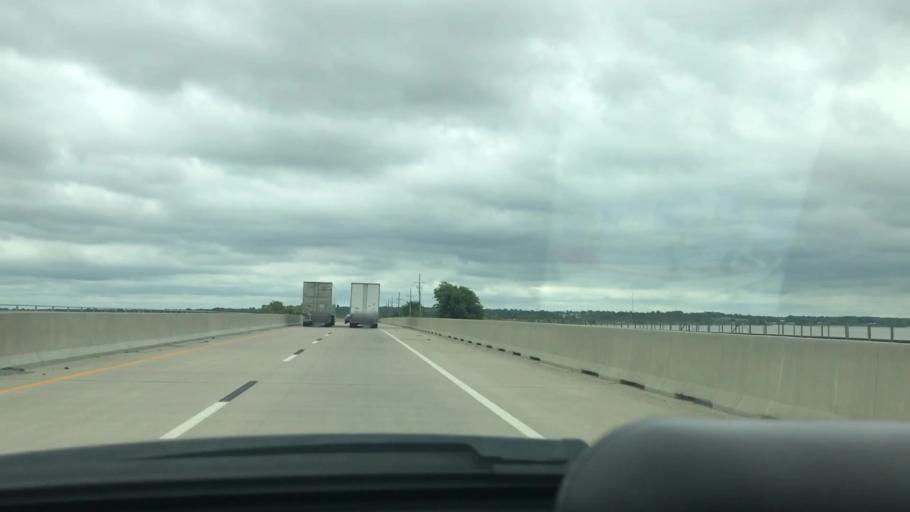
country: US
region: Oklahoma
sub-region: McIntosh County
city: Eufaula
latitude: 35.3311
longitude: -95.5868
